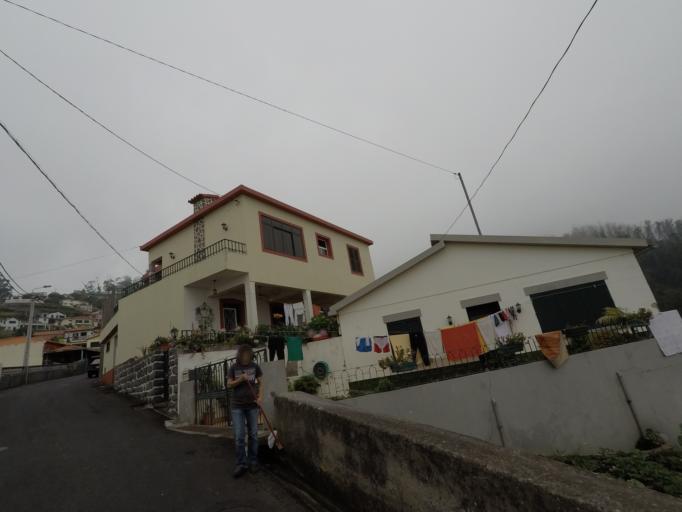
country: PT
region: Madeira
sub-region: Camara de Lobos
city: Curral das Freiras
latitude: 32.6836
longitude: -16.9470
